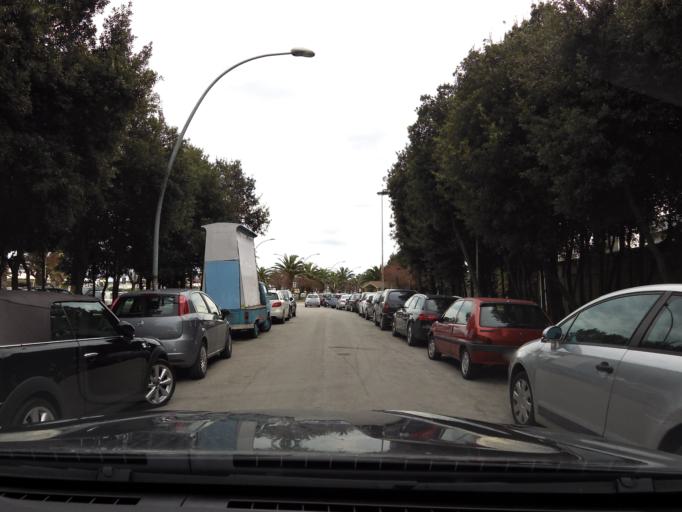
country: IT
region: The Marches
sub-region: Provincia di Macerata
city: Portocivitanova
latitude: 43.3089
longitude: 13.7330
